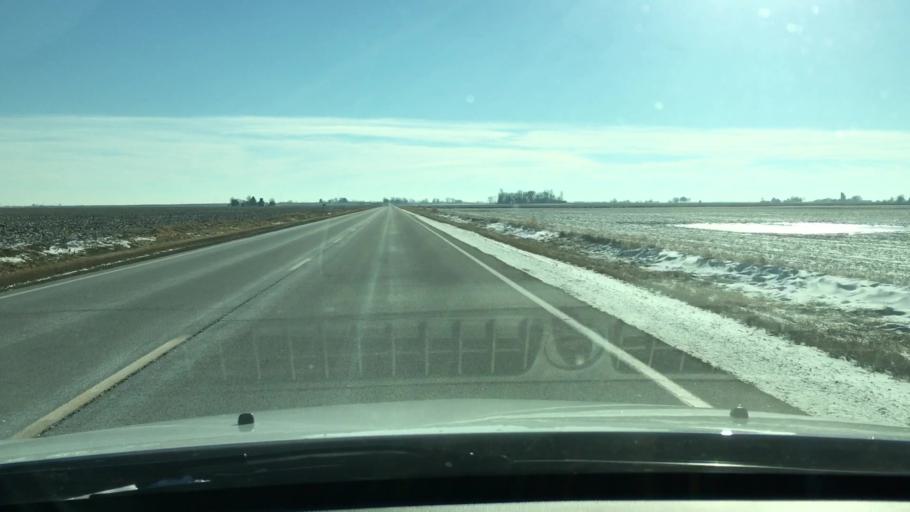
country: US
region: Illinois
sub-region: Ogle County
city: Rochelle
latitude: 41.8607
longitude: -89.0732
